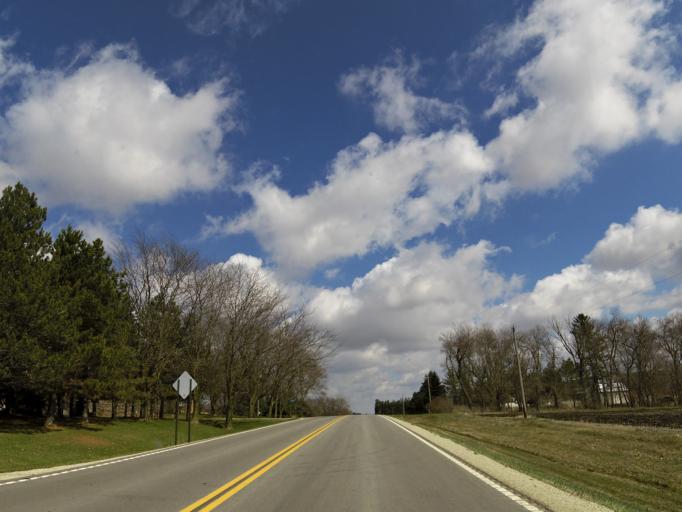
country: US
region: Minnesota
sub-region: Dodge County
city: Dodge Center
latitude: 44.0881
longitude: -92.8968
